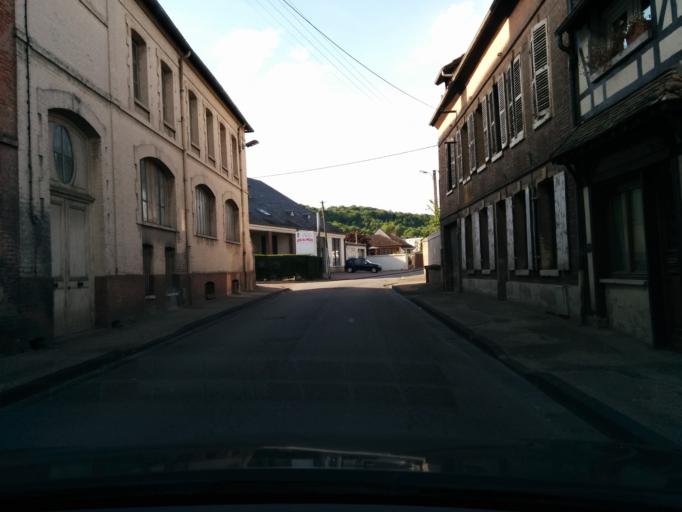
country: FR
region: Haute-Normandie
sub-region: Departement de l'Eure
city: Les Andelys
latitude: 49.2486
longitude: 1.4135
